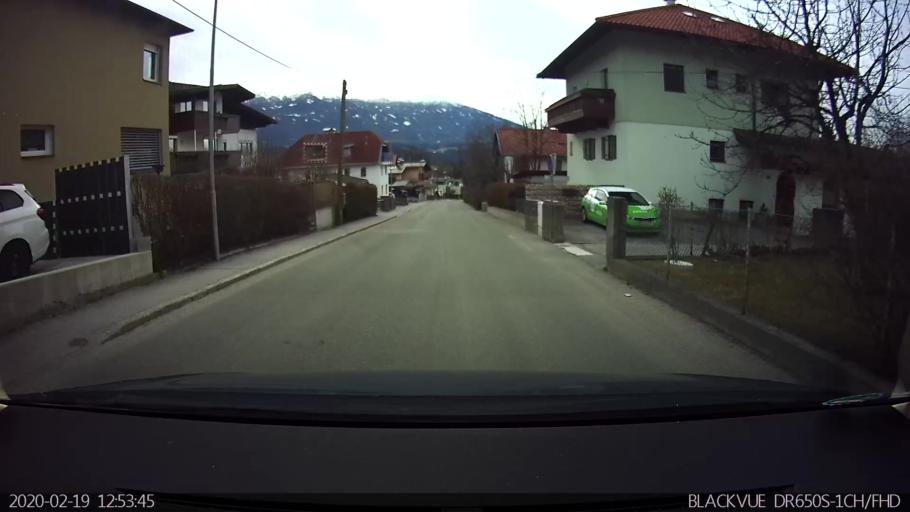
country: AT
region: Tyrol
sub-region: Politischer Bezirk Innsbruck Land
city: Absam
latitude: 47.3032
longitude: 11.5147
